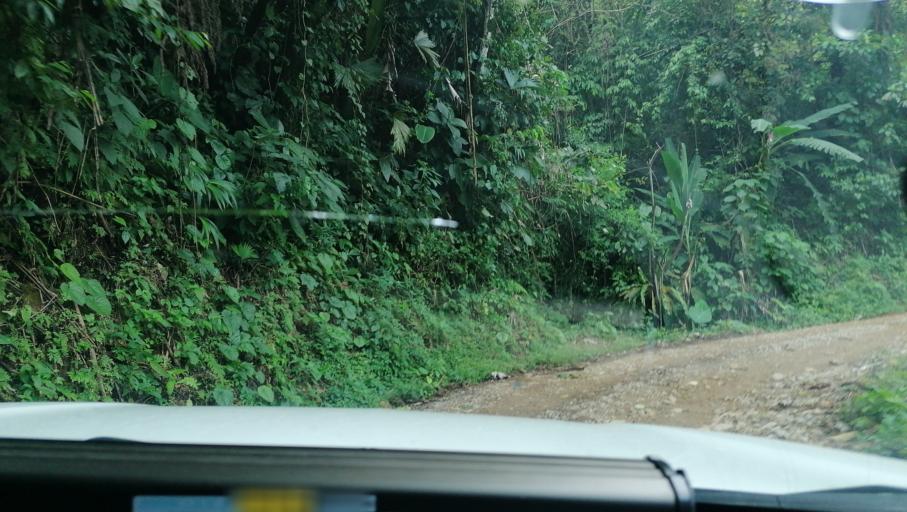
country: MX
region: Chiapas
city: Ixtacomitan
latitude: 17.3351
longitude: -93.1094
